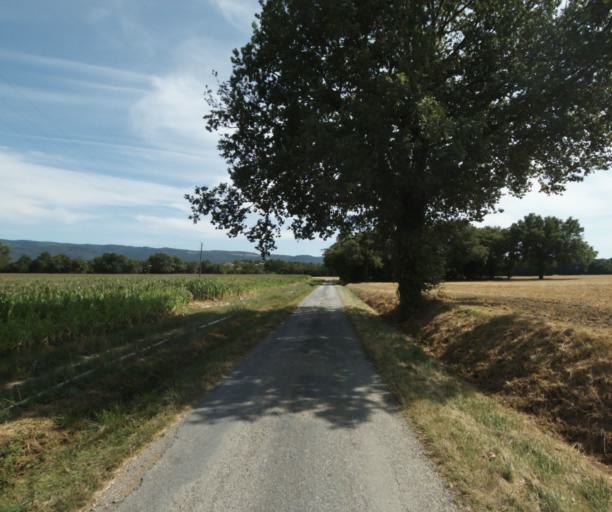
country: FR
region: Midi-Pyrenees
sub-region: Departement du Tarn
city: Soreze
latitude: 43.5050
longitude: 2.0631
